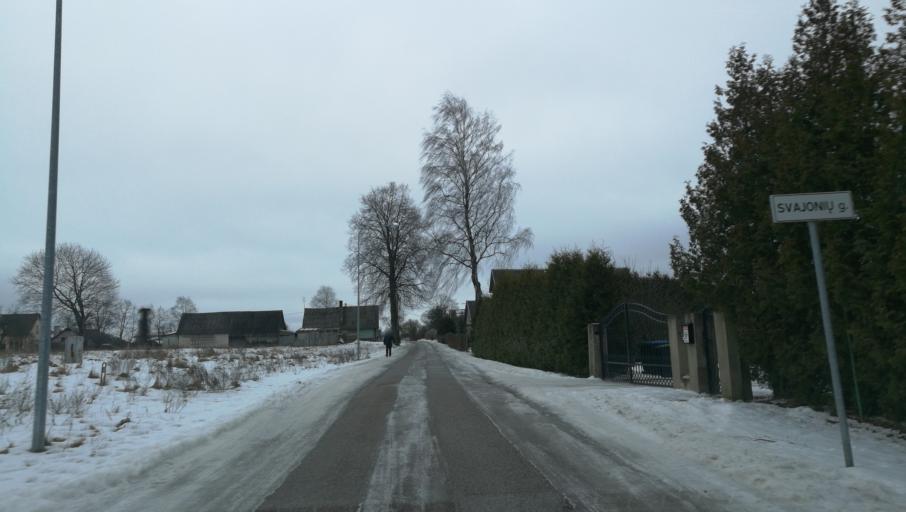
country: LT
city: Trakai
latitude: 54.6165
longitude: 24.9192
